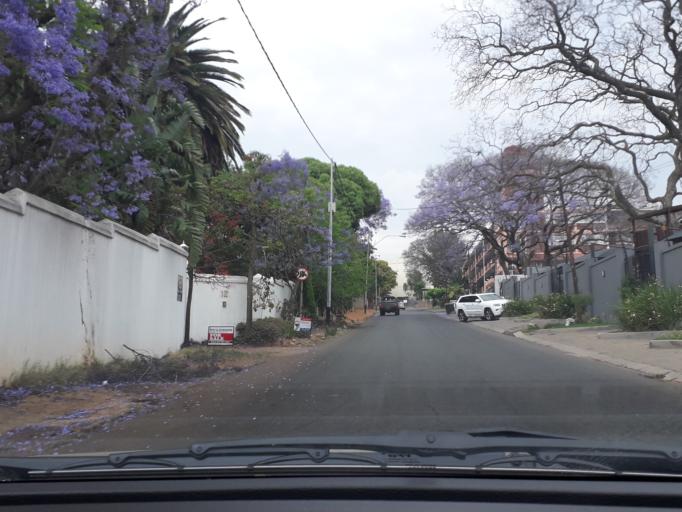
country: ZA
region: Gauteng
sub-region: City of Johannesburg Metropolitan Municipality
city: Modderfontein
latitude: -26.1332
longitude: 28.0939
